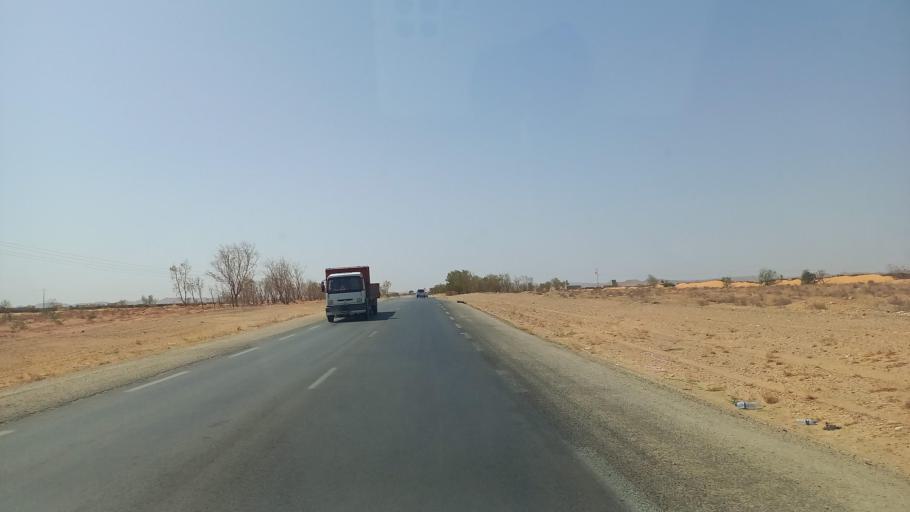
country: TN
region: Madanin
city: Medenine
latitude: 33.2166
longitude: 10.4482
